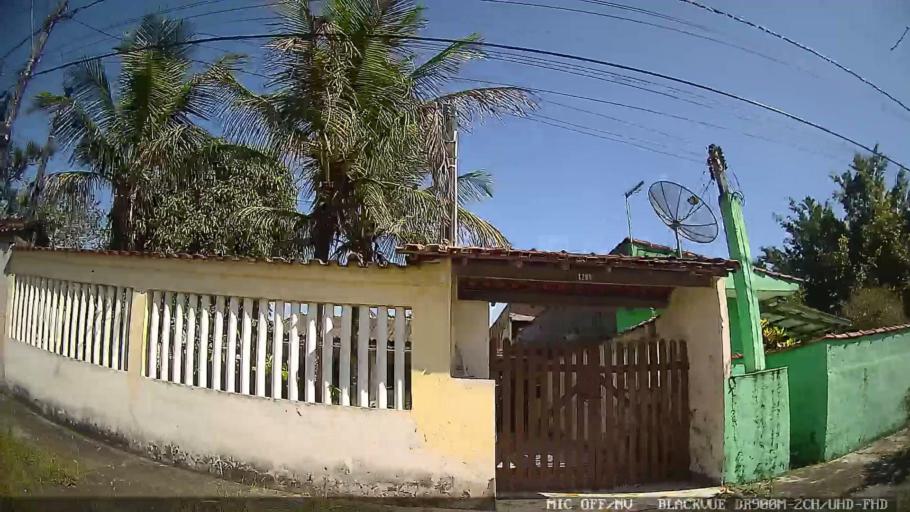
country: BR
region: Sao Paulo
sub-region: Itanhaem
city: Itanhaem
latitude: -24.1470
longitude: -46.7396
